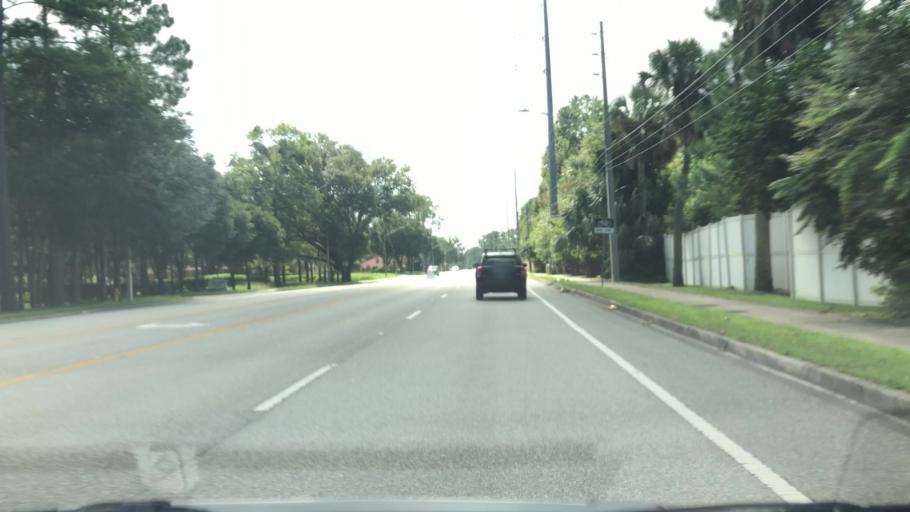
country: US
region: Florida
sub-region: Saint Johns County
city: Fruit Cove
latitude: 30.1580
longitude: -81.5963
